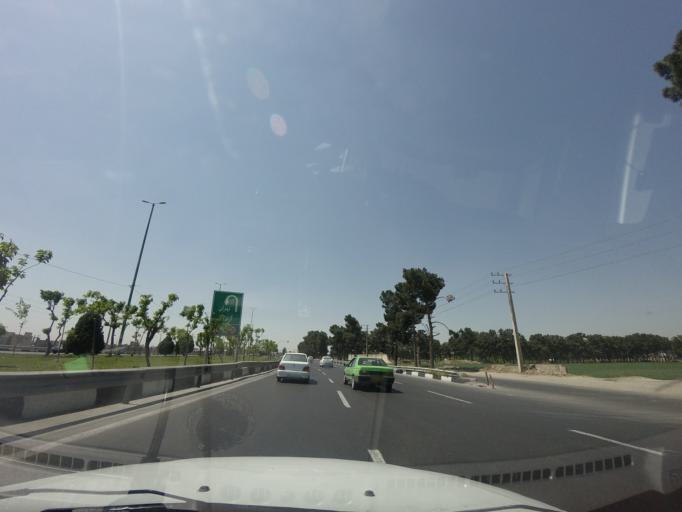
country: IR
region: Tehran
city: Eslamshahr
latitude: 35.5818
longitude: 51.2728
